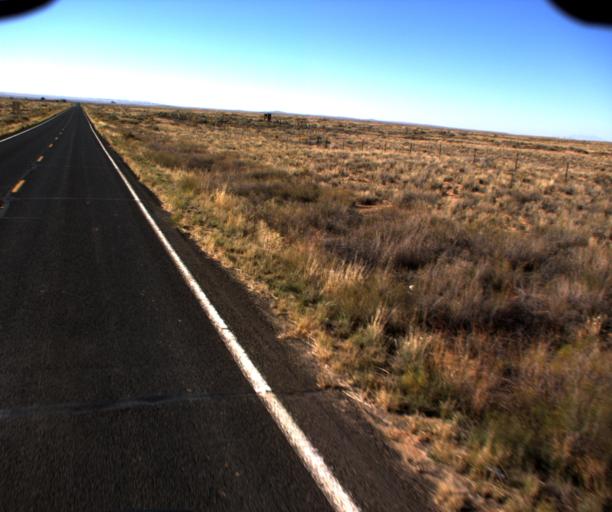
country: US
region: Arizona
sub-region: Navajo County
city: First Mesa
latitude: 35.7861
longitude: -110.4993
